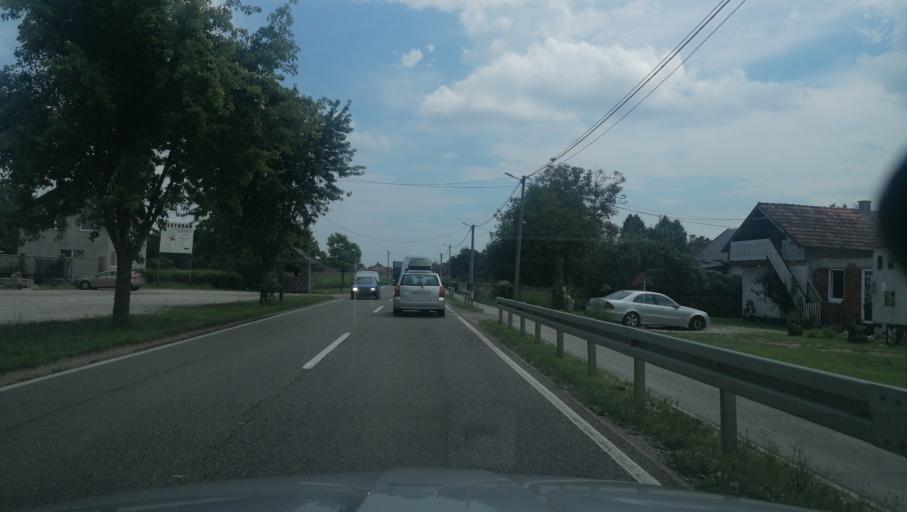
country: BA
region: Republika Srpska
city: Obudovac
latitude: 44.9588
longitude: 18.6282
